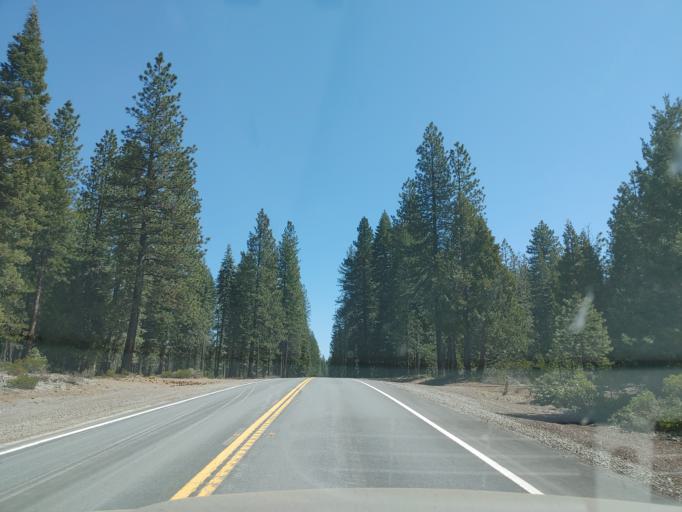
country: US
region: California
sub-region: Siskiyou County
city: McCloud
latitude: 41.2664
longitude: -121.9238
